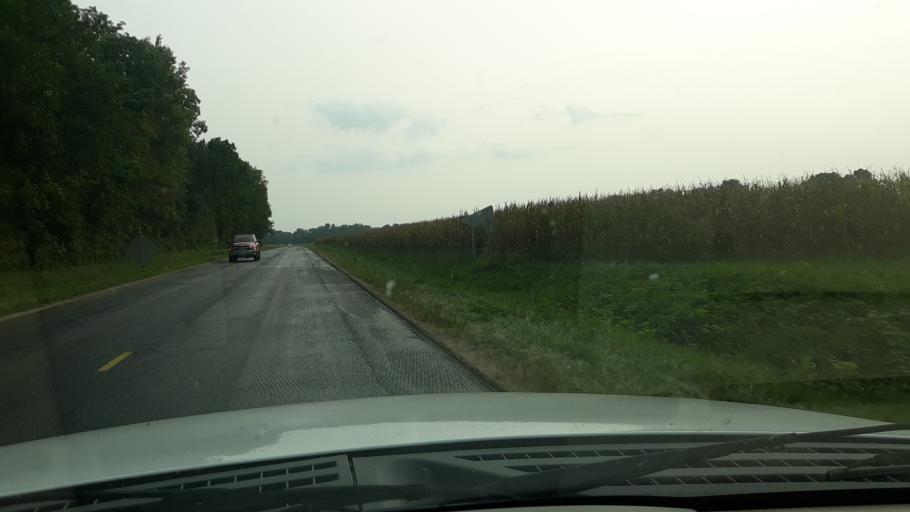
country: US
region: Illinois
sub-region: Edwards County
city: Grayville
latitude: 38.2848
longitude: -87.9809
